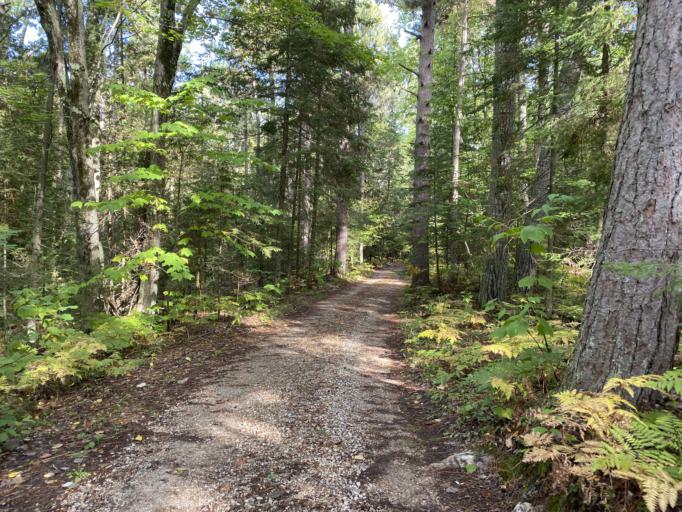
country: US
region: Michigan
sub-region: Mackinac County
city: Saint Ignace
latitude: 45.7478
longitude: -84.8794
